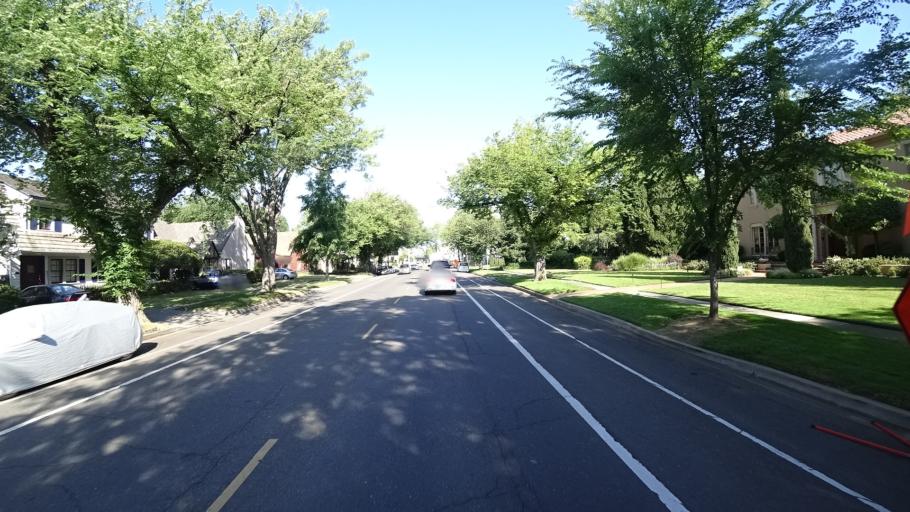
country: US
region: California
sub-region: Sacramento County
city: Sacramento
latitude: 38.5590
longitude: -121.4604
